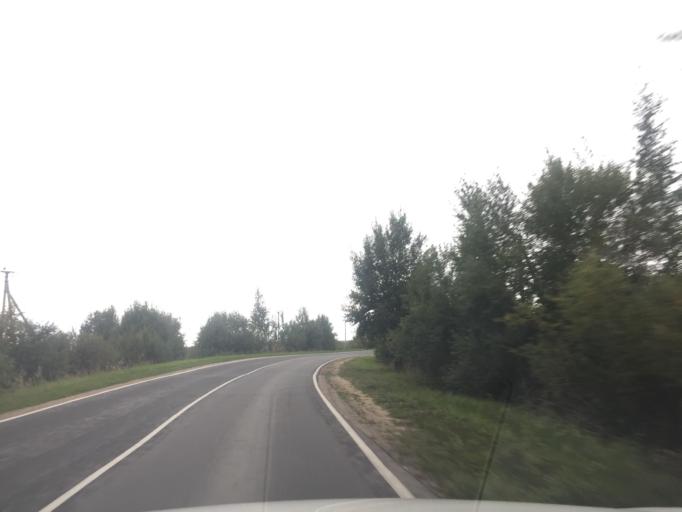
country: RU
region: Leningrad
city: Siverskiy
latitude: 59.3308
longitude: 30.0304
